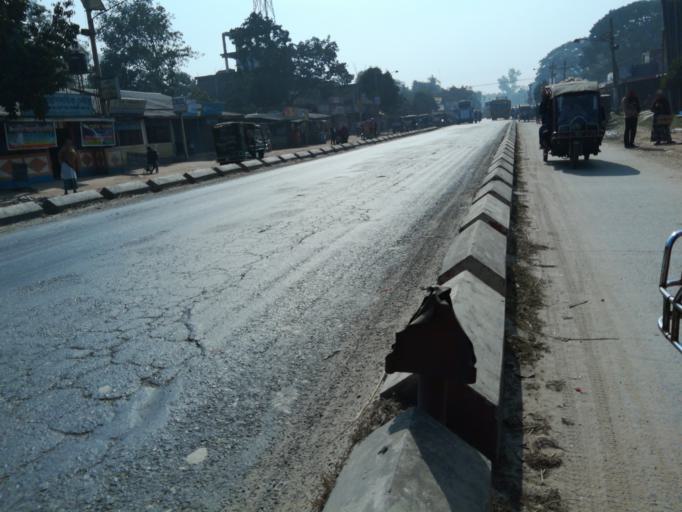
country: BD
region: Rangpur Division
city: Rangpur
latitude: 25.5717
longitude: 89.2744
